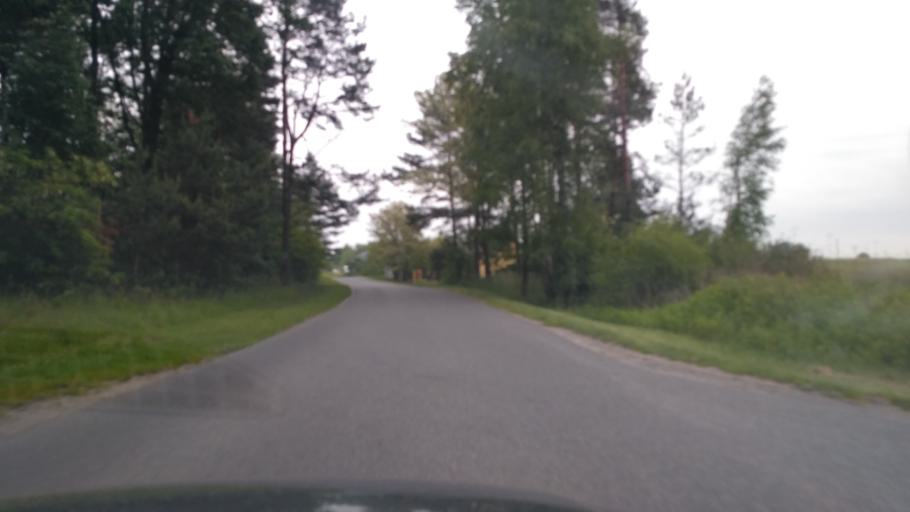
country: PL
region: Subcarpathian Voivodeship
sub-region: Powiat kolbuszowski
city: Niwiska
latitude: 50.1746
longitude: 21.6645
